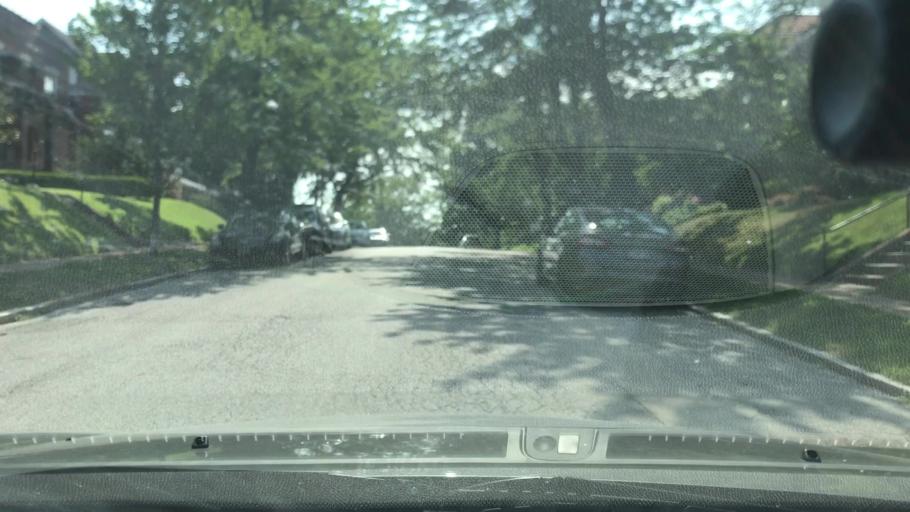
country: US
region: Missouri
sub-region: Saint Louis County
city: Richmond Heights
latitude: 38.6125
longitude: -90.2902
